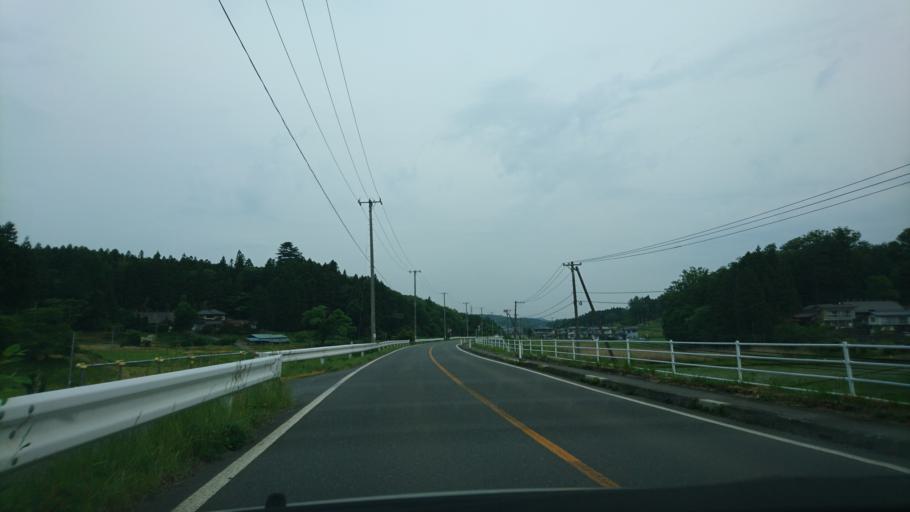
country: JP
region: Iwate
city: Ichinoseki
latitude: 38.8872
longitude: 141.1331
